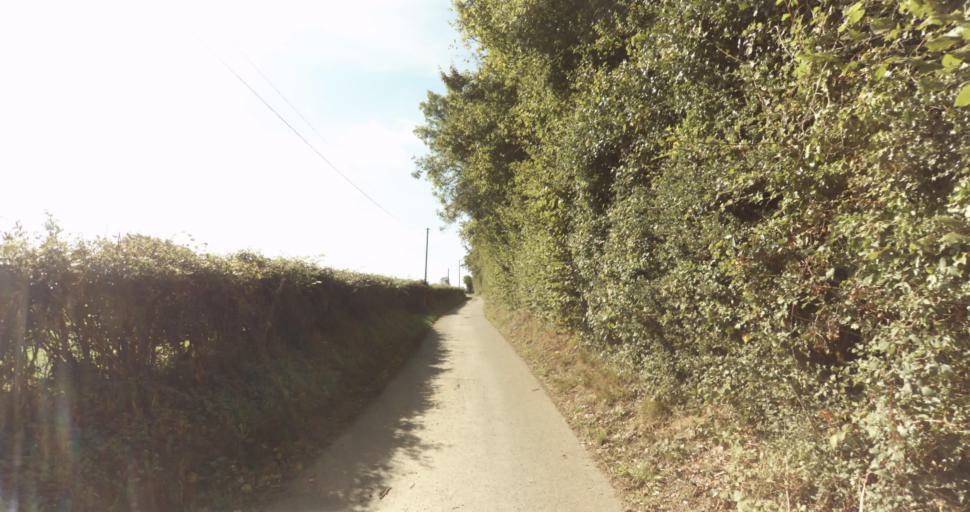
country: FR
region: Lower Normandy
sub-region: Departement de l'Orne
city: Vimoutiers
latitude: 48.9167
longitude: 0.3119
